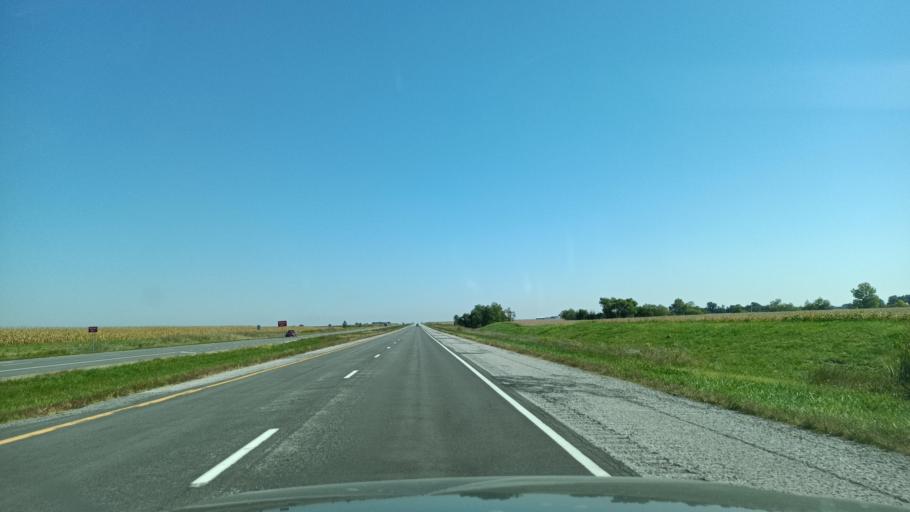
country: US
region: Illinois
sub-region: Adams County
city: Camp Point
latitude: 40.1989
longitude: -91.1545
